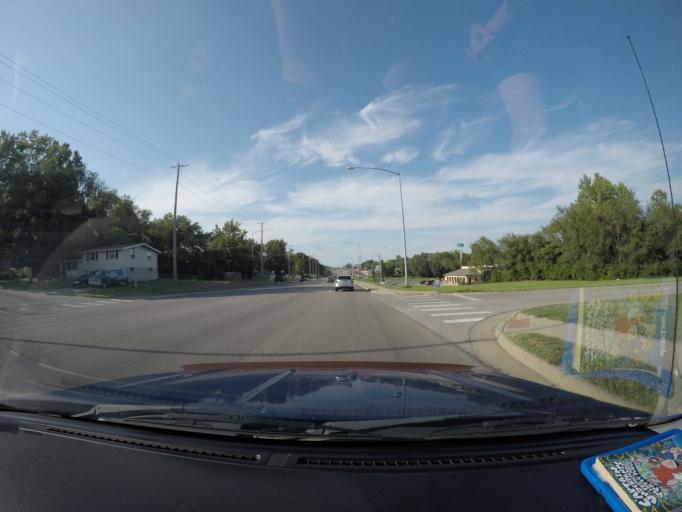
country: US
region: Kansas
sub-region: Leavenworth County
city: Lansing
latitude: 39.2599
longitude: -94.8999
